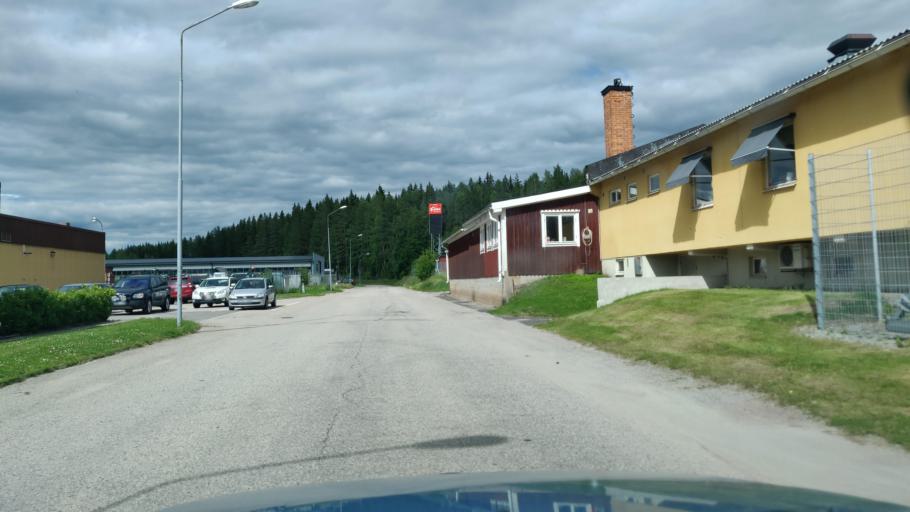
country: SE
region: Vaermland
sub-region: Hagfors Kommun
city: Hagfors
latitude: 60.0431
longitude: 13.7114
